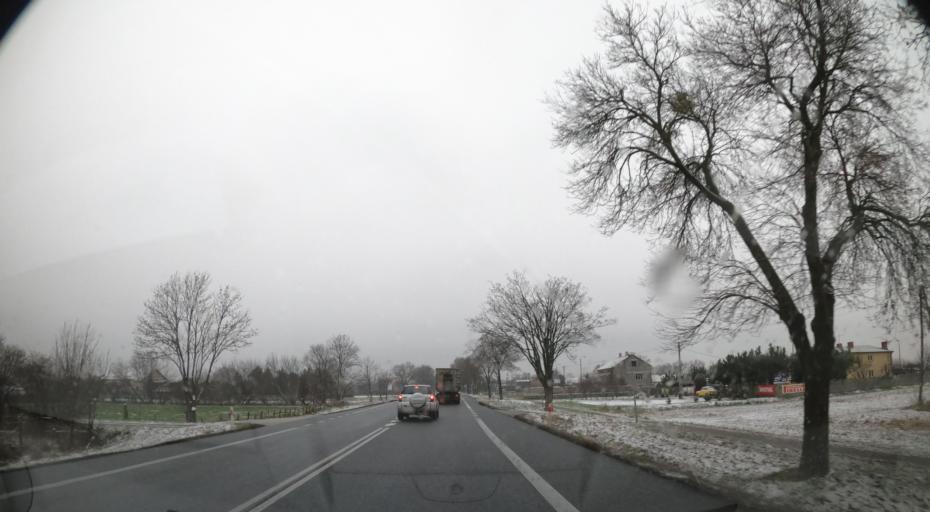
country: PL
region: Masovian Voivodeship
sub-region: Powiat sochaczewski
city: Teresin
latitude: 52.2201
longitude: 20.3410
